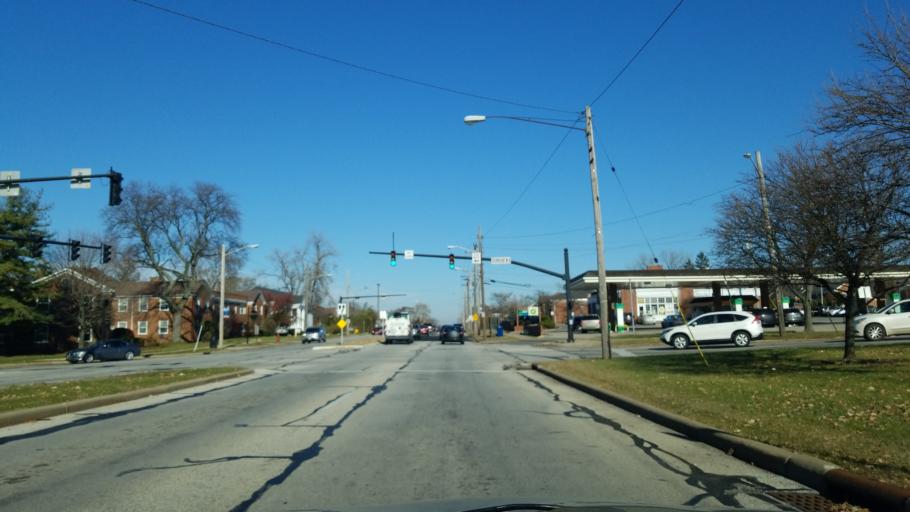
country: US
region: Ohio
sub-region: Cuyahoga County
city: University Heights
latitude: 41.4867
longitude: -81.5362
